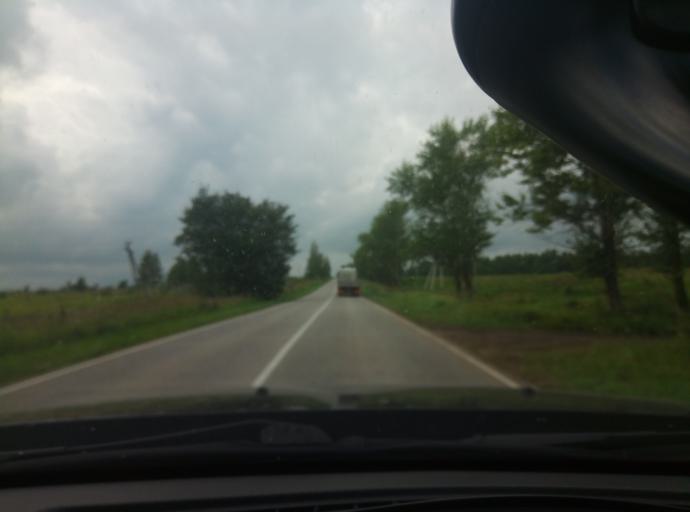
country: RU
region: Tula
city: Priupskiy
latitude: 53.9730
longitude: 37.7400
